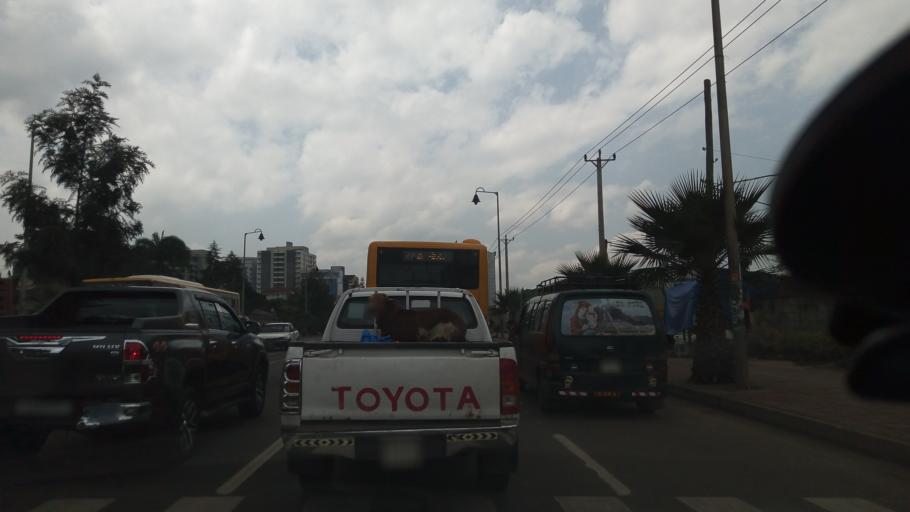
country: ET
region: Adis Abeba
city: Addis Ababa
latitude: 8.9904
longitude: 38.7204
